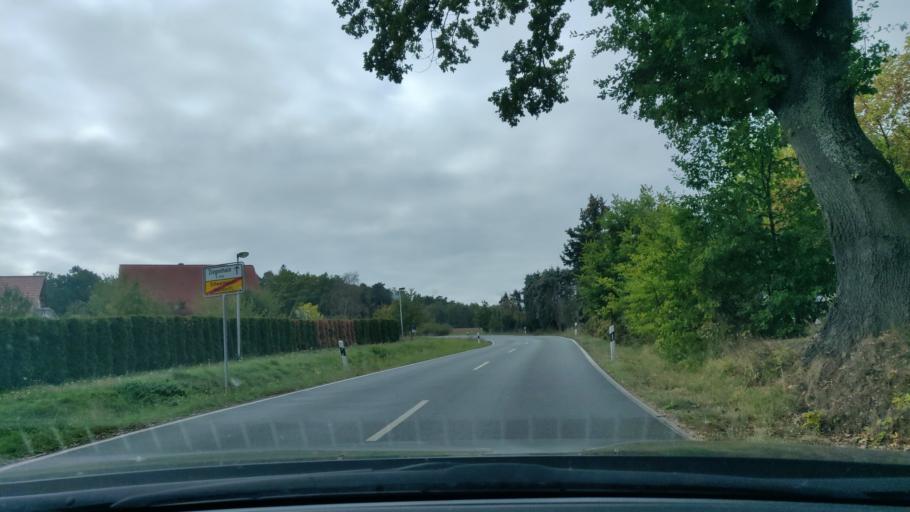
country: DE
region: Hesse
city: Schwalmstadt
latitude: 50.9447
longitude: 9.2130
